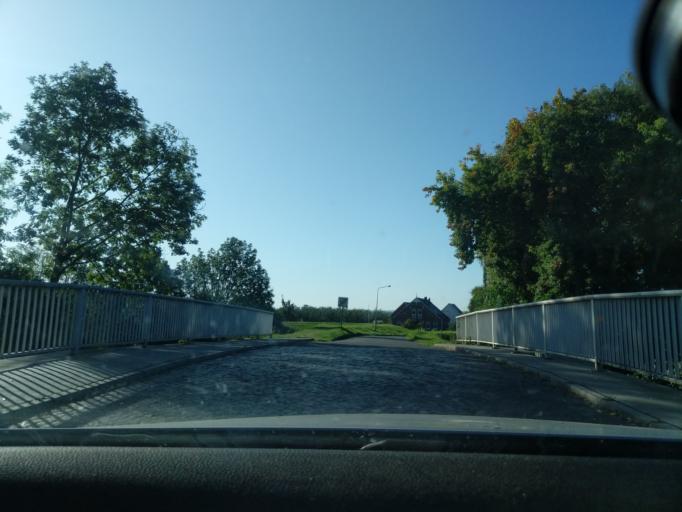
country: DE
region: Lower Saxony
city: Grunendeich
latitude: 53.5676
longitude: 9.6267
